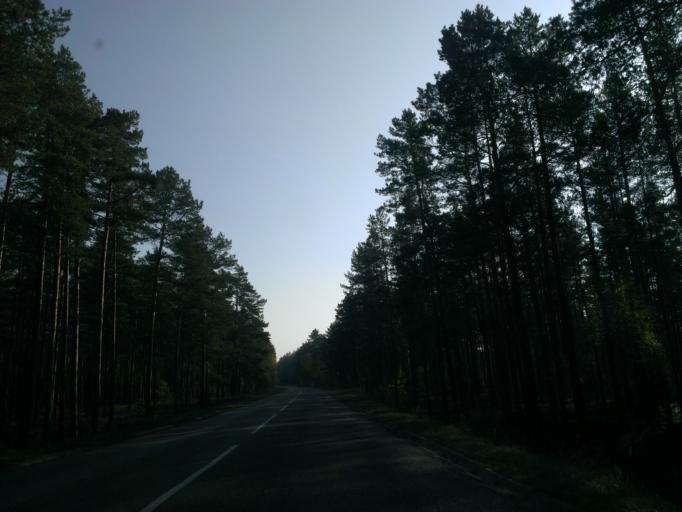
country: LV
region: Garkalne
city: Garkalne
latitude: 57.0375
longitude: 24.4169
